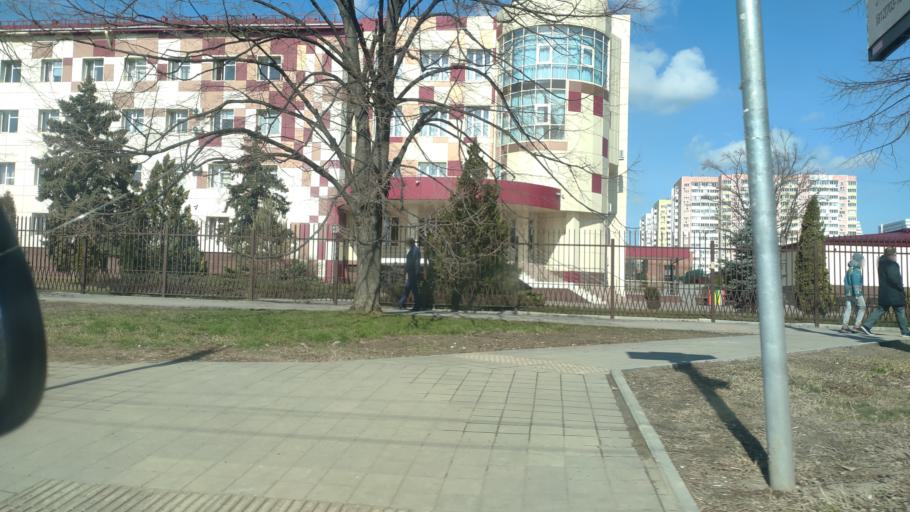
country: RU
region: Krasnodarskiy
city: Krasnodar
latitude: 45.0554
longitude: 39.0058
